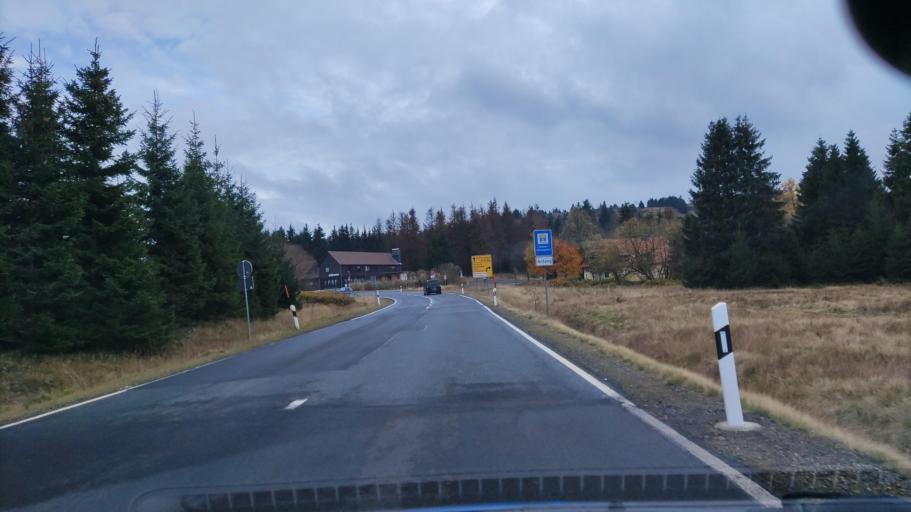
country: DE
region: Lower Saxony
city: Sankt Andreasberg
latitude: 51.7620
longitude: 10.5115
